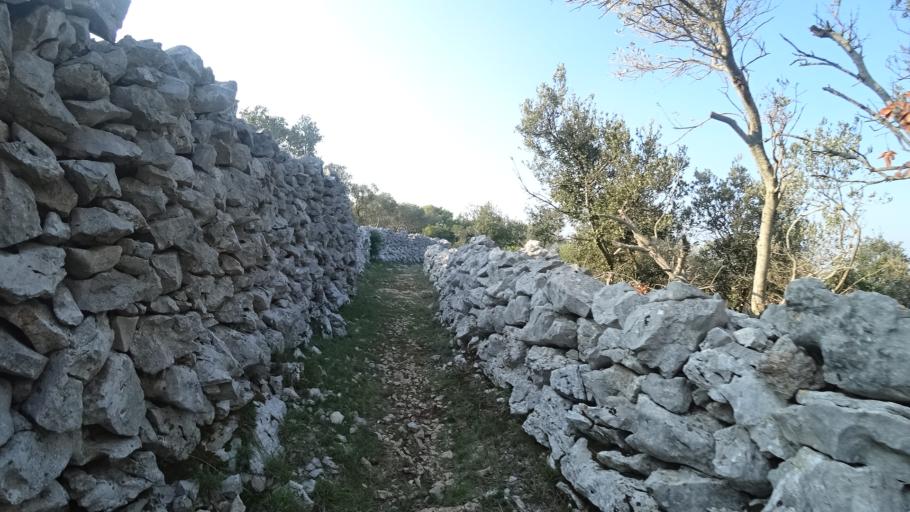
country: HR
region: Primorsko-Goranska
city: Mali Losinj
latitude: 44.5235
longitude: 14.4761
